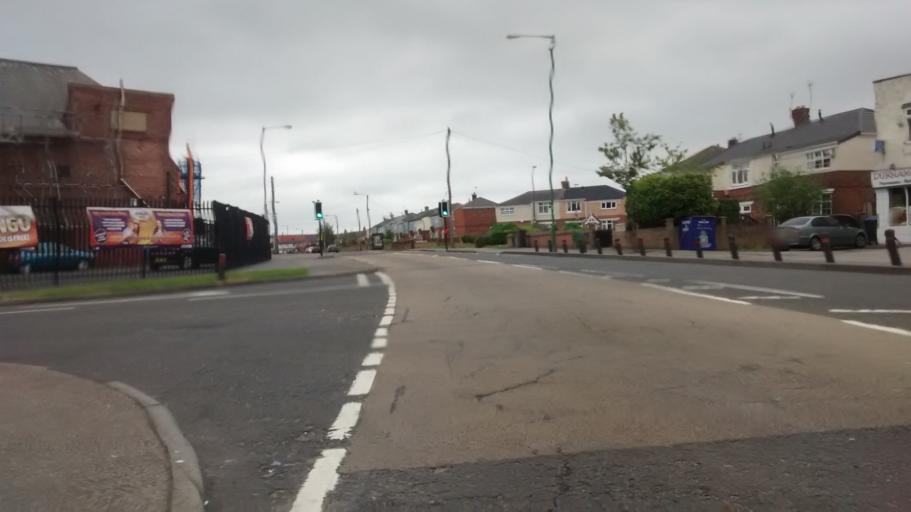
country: GB
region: England
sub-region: County Durham
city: Durham
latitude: 54.7768
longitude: -1.5454
